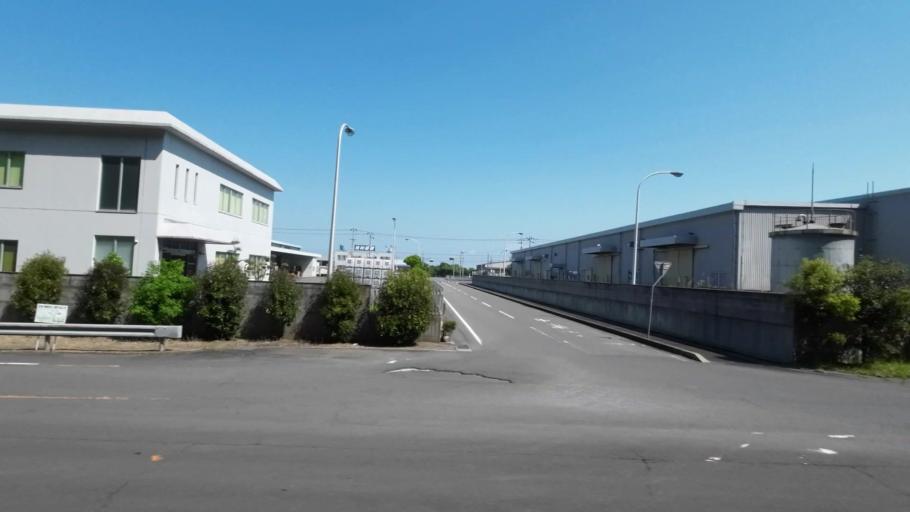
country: JP
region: Ehime
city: Kawanoecho
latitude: 34.0414
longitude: 133.6053
